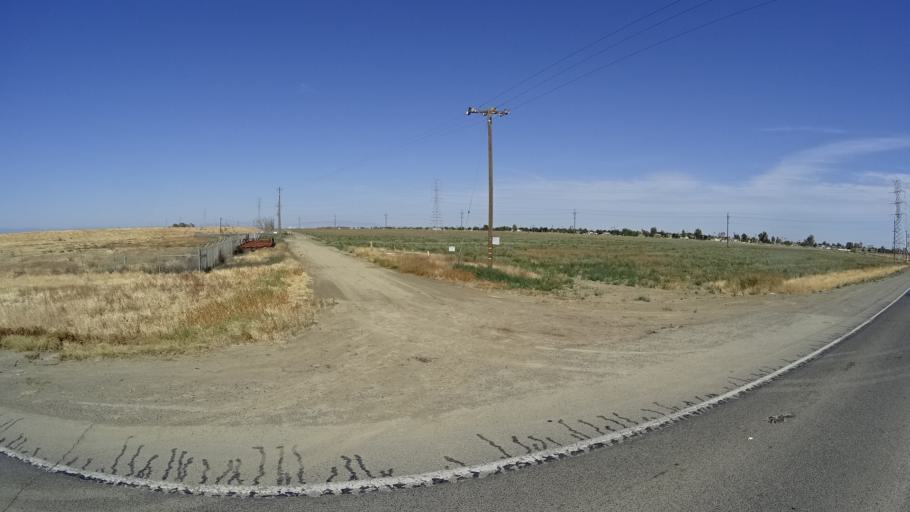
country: US
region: California
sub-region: Kings County
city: Lemoore Station
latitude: 36.2504
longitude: -119.8695
